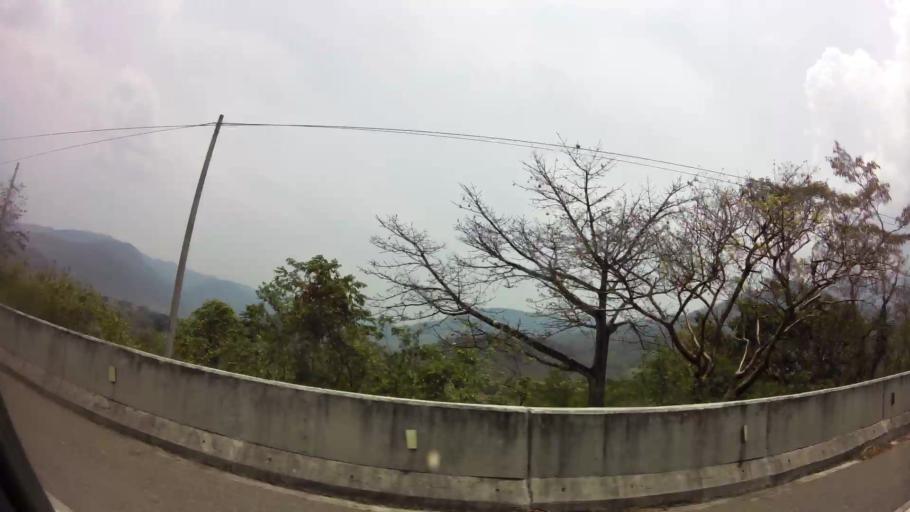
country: HN
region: Comayagua
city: Taulabe
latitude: 14.6952
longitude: -87.9528
